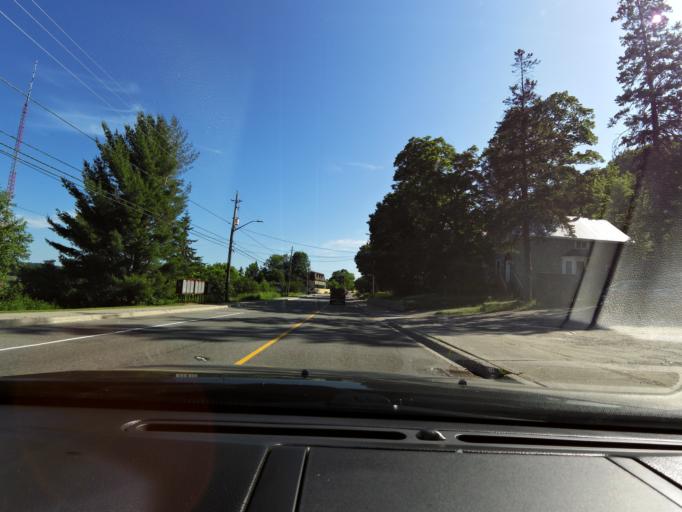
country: CA
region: Ontario
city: Huntsville
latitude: 45.3228
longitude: -79.2262
